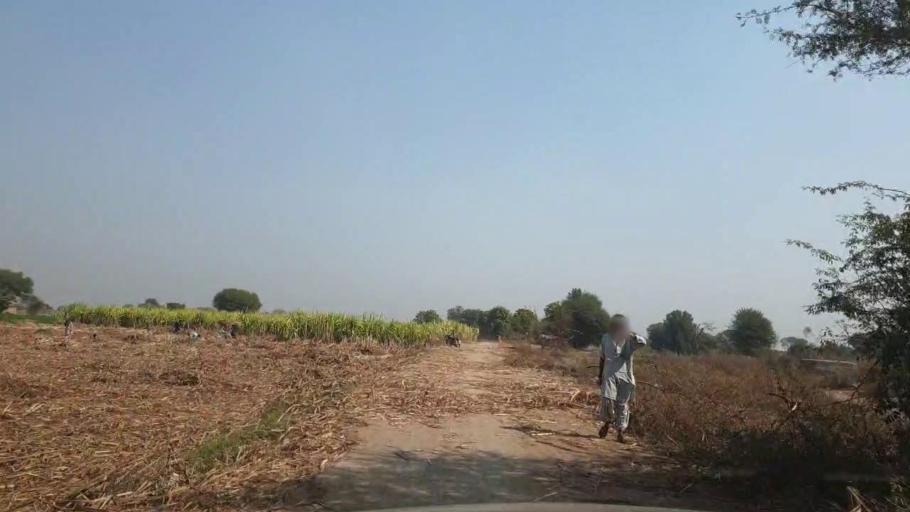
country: PK
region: Sindh
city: Tando Allahyar
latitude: 25.5541
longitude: 68.7250
